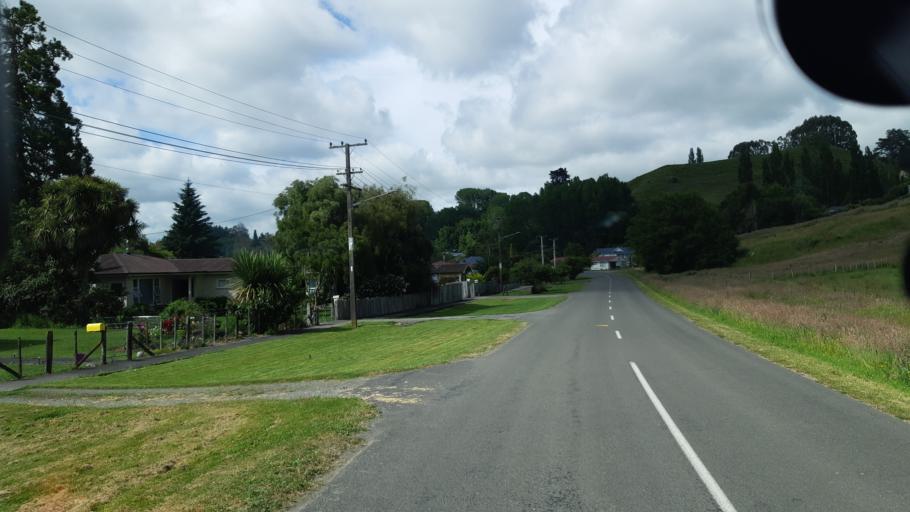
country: NZ
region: Manawatu-Wanganui
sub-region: Rangitikei District
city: Bulls
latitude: -39.9296
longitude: 175.5644
